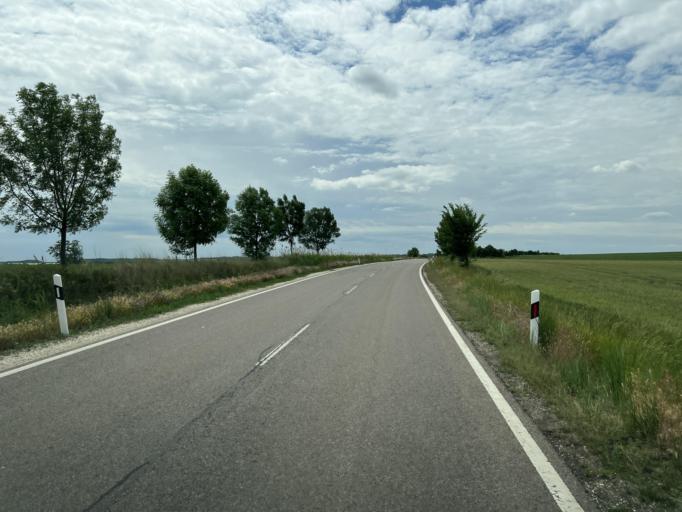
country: HU
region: Pest
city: Zsambok
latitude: 47.5195
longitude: 19.5998
